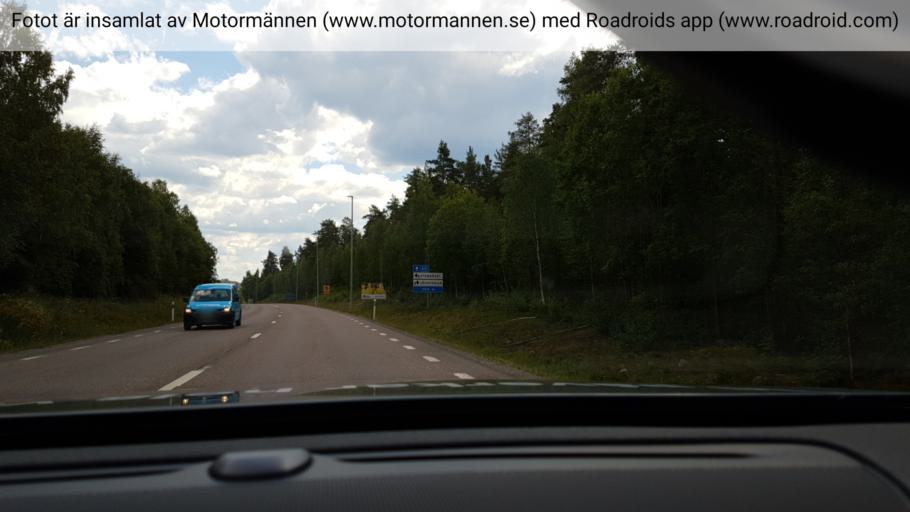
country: SE
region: Dalarna
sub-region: Faluns Kommun
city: Falun
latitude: 60.6309
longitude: 15.5961
